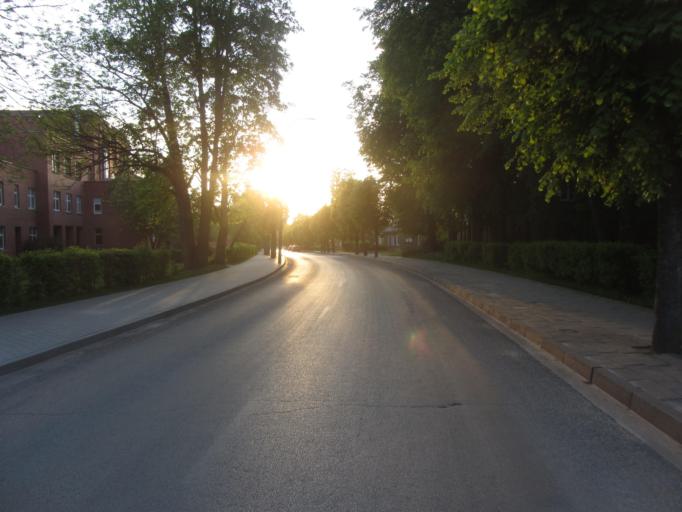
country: LT
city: Sirvintos
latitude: 55.0386
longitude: 24.9642
